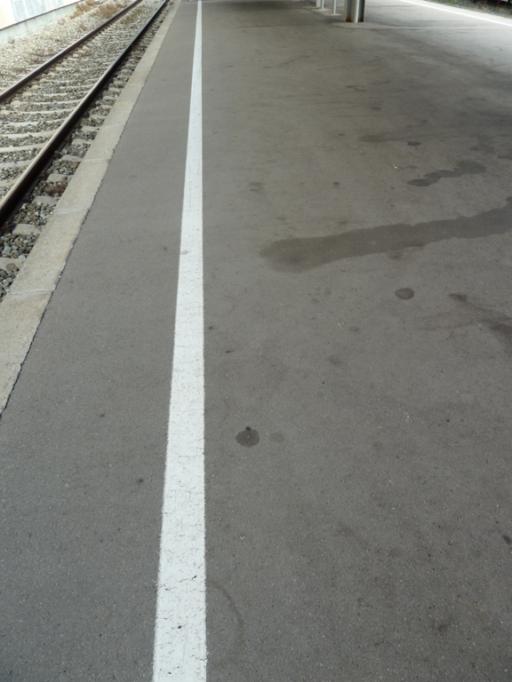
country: DE
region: Baden-Wuerttemberg
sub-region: Tuebingen Region
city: Friedrichshafen
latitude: 47.6513
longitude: 9.4825
